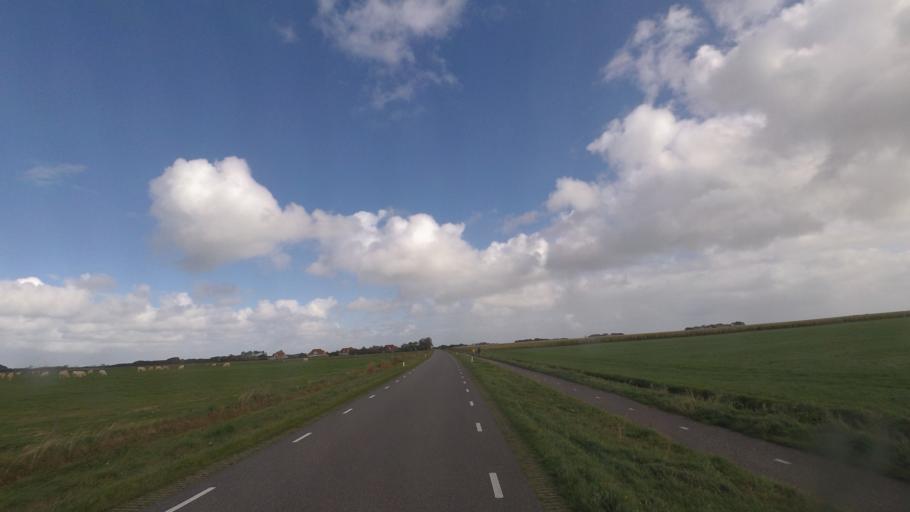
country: NL
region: Friesland
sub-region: Gemeente Ameland
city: Hollum
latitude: 53.4377
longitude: 5.6481
